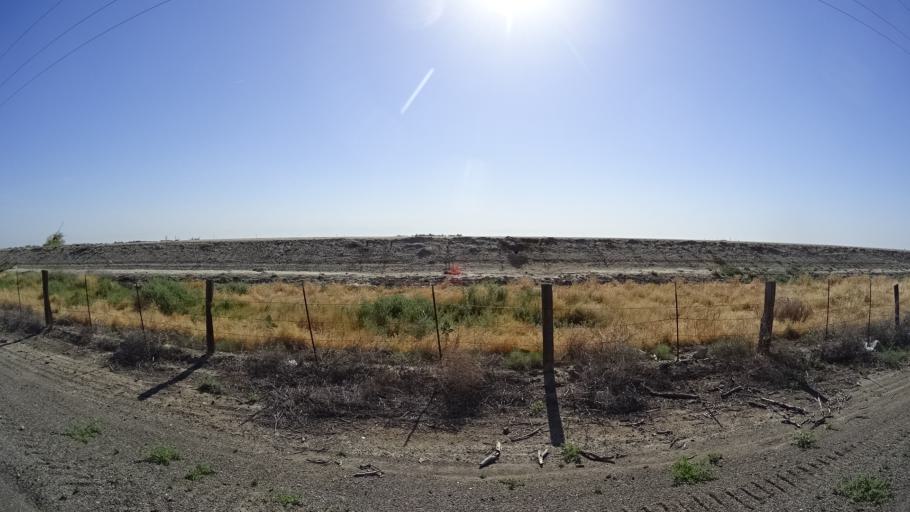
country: US
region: California
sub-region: Kings County
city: Corcoran
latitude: 36.1561
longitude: -119.5649
